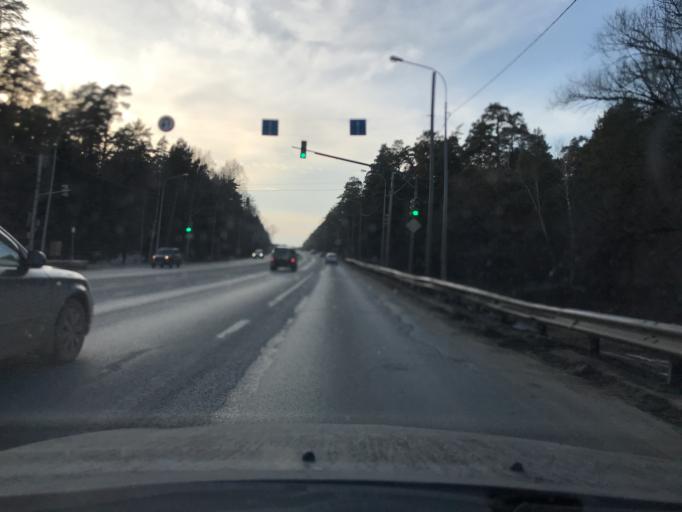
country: RU
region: Kaluga
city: Mstikhino
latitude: 54.5221
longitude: 36.1930
